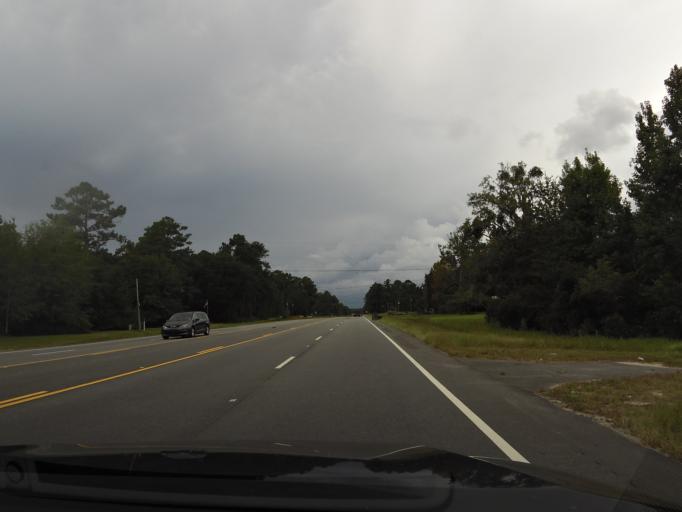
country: US
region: Georgia
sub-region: Glynn County
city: Dock Junction
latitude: 31.2850
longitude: -81.5660
